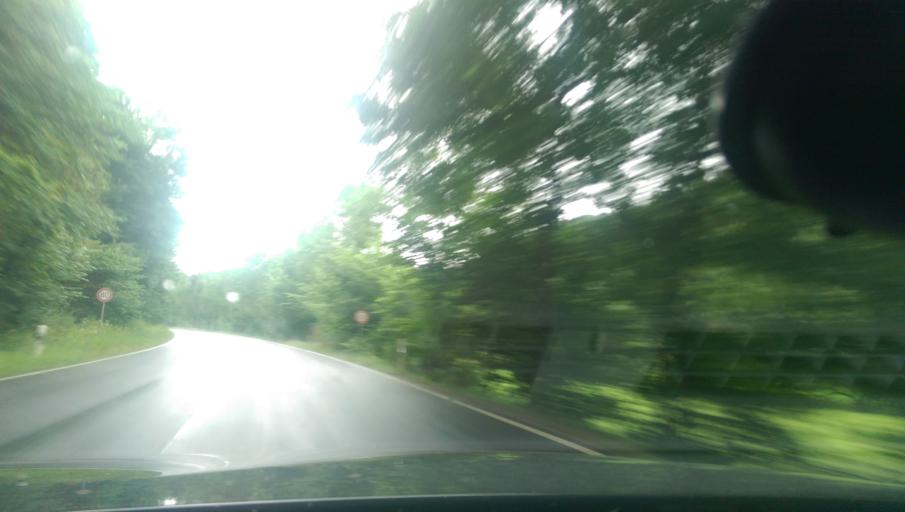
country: DE
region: Hesse
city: Witzenhausen
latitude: 51.3050
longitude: 9.8529
